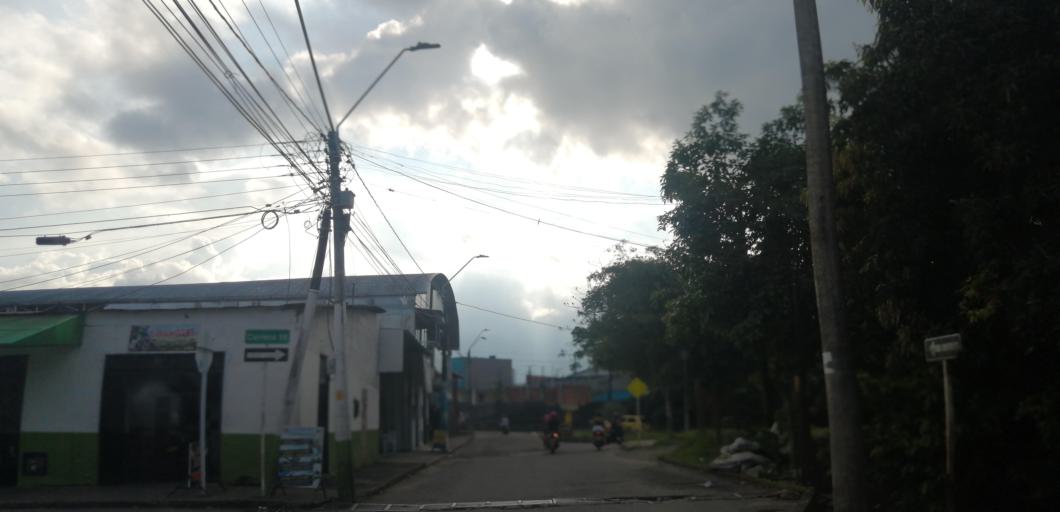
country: CO
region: Meta
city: Acacias
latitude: 3.9886
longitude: -73.7620
